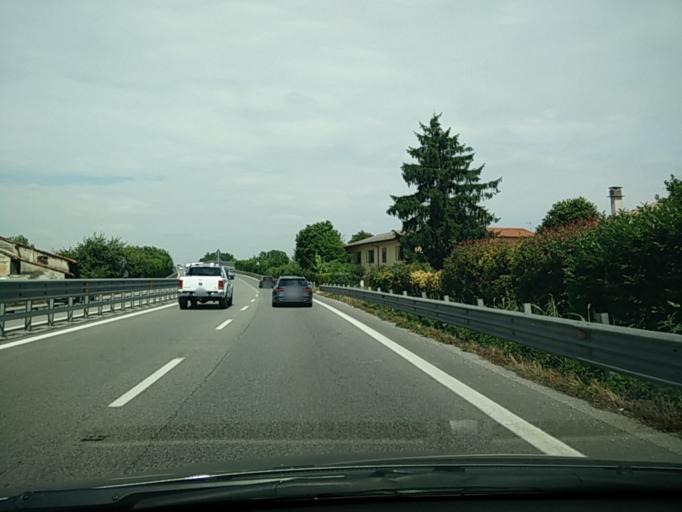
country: IT
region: Veneto
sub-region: Provincia di Venezia
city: Campalto
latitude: 45.5116
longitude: 12.2603
